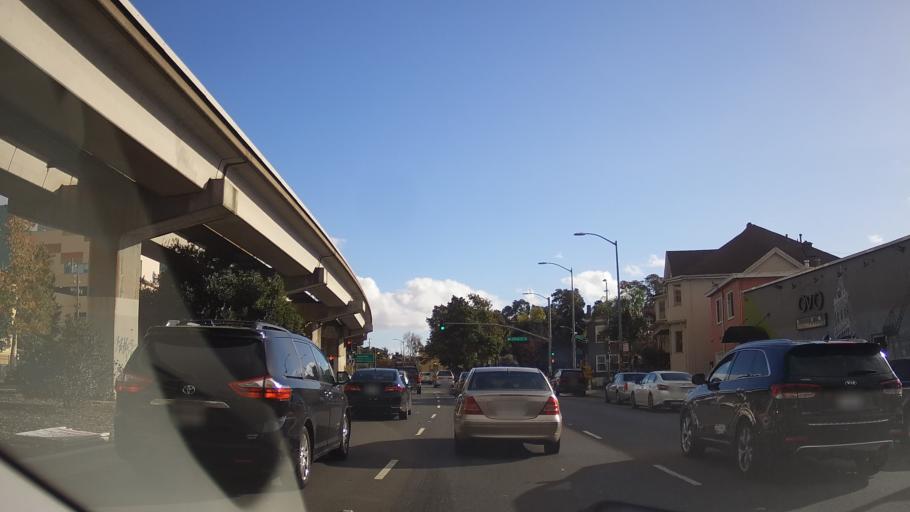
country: US
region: California
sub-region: Alameda County
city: Emeryville
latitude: 37.8386
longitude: -122.2695
